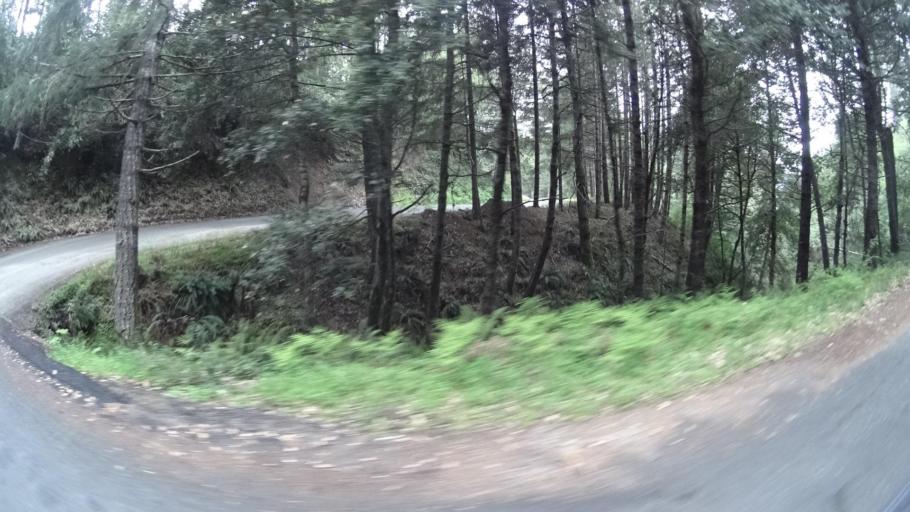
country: US
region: California
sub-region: Humboldt County
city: Redway
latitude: 40.2723
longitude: -123.7728
